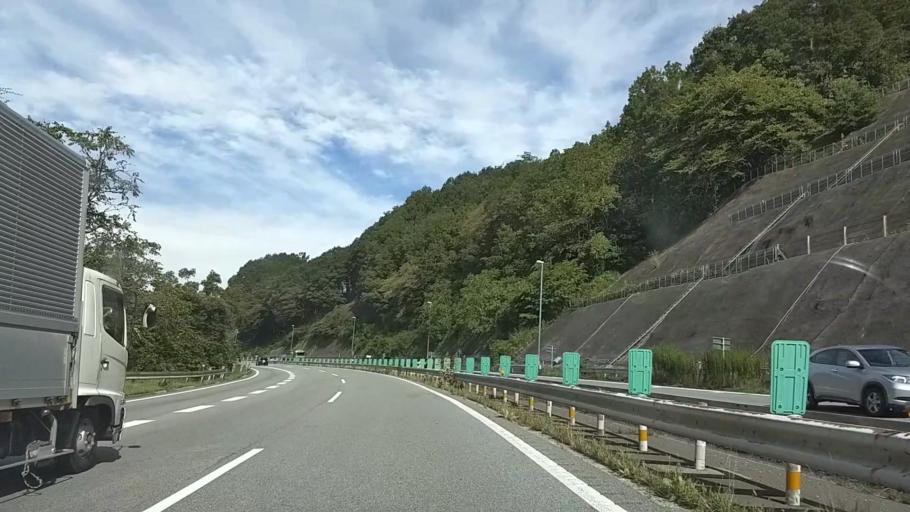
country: JP
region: Yamanashi
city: Nirasaki
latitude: 35.7902
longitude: 138.4092
